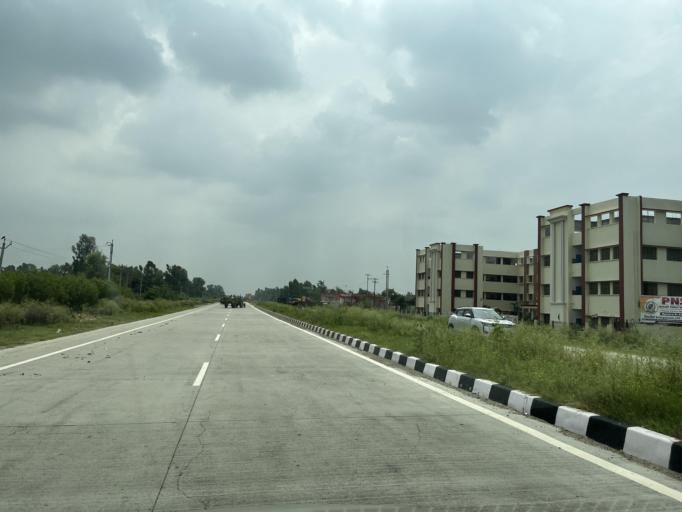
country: IN
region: Uttar Pradesh
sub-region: Bijnor
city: Najibabad
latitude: 29.5619
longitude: 78.3389
